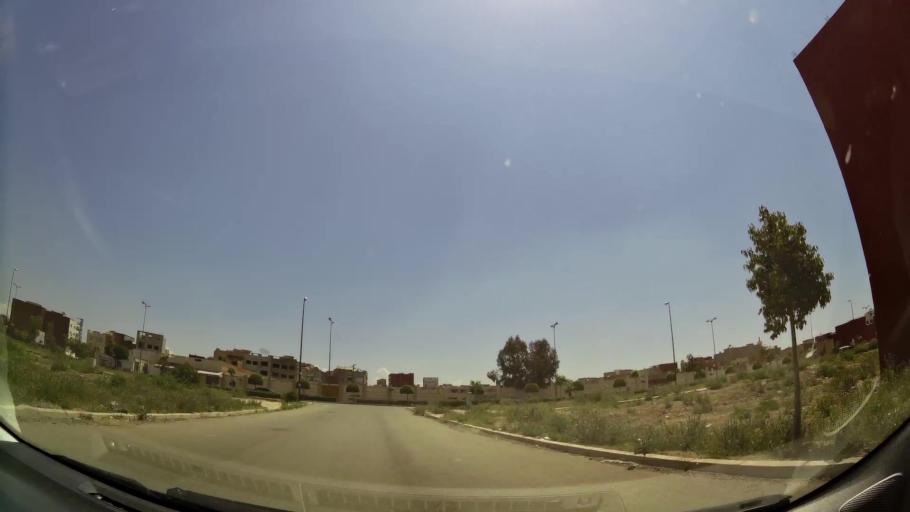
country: MA
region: Oriental
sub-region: Oujda-Angad
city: Oujda
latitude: 34.6838
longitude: -1.9482
